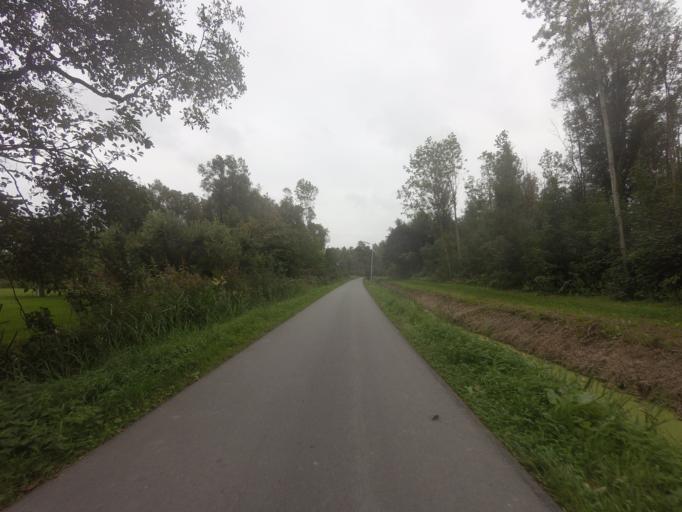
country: NL
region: Friesland
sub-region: Gemeente Leeuwarden
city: Bilgaard
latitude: 53.2222
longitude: 5.7898
